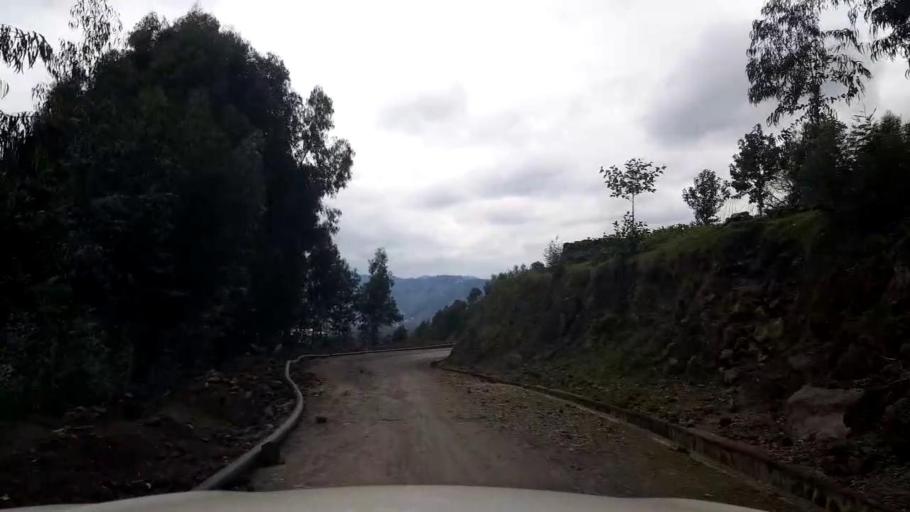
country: RW
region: Northern Province
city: Musanze
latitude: -1.5346
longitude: 29.5330
